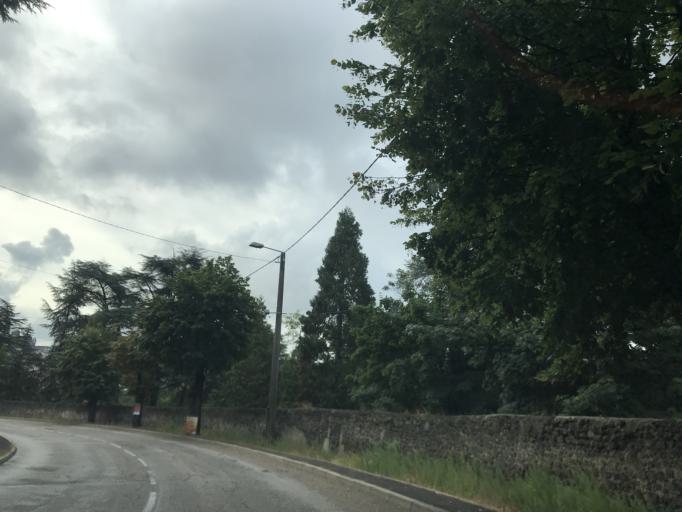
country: FR
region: Auvergne
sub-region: Departement de la Haute-Loire
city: Espaly-Saint-Marcel
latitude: 45.0499
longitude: 3.8714
